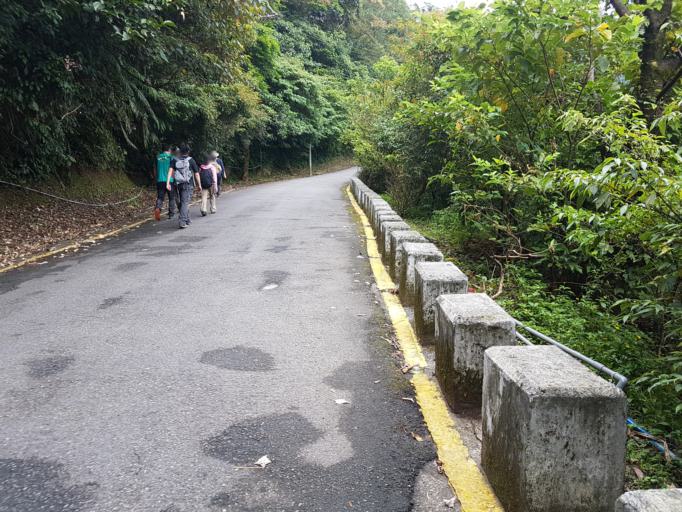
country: TW
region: Taiwan
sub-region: Keelung
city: Keelung
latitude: 25.0517
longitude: 121.6648
